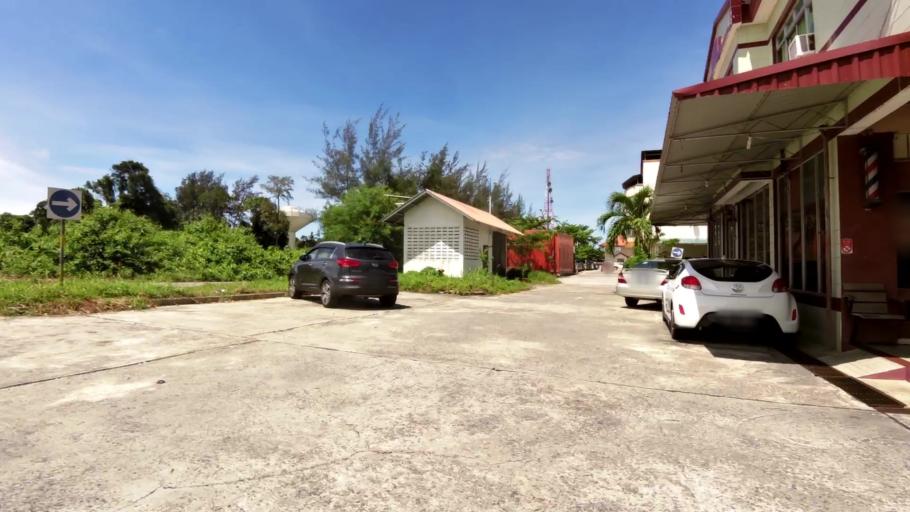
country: BN
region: Belait
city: Kuala Belait
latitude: 4.5904
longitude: 114.2285
